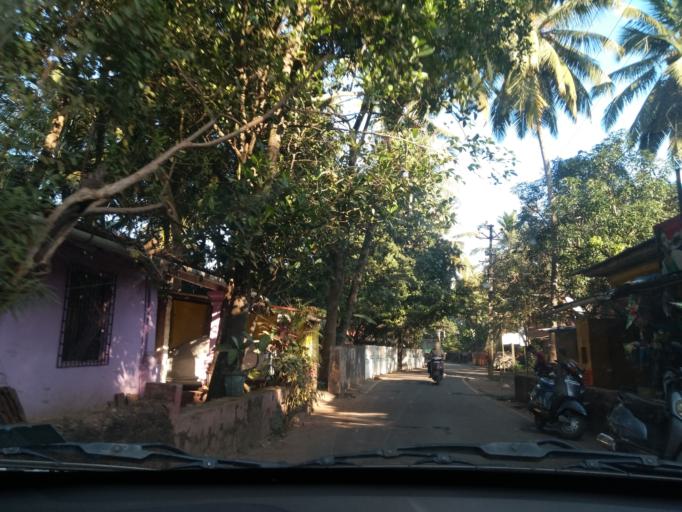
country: IN
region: Goa
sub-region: South Goa
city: Madgaon
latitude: 15.2537
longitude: 73.9560
